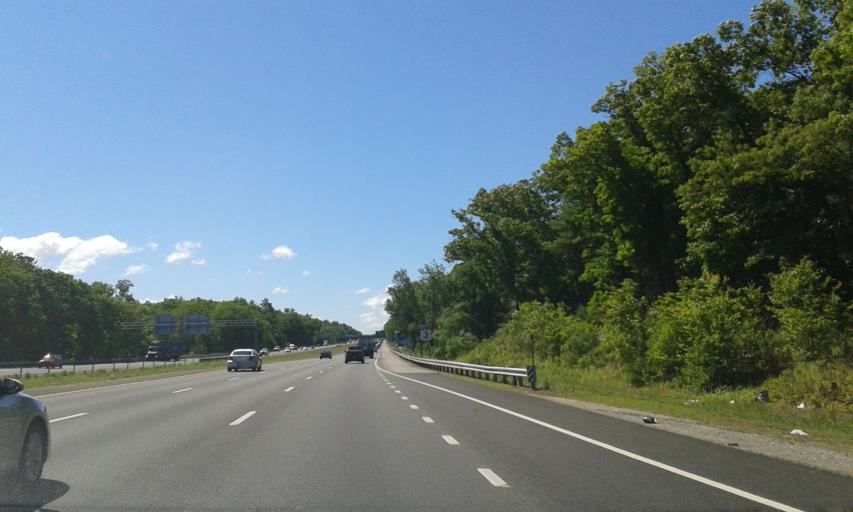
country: US
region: Massachusetts
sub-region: Middlesex County
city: Billerica
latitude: 42.5843
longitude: -71.3098
